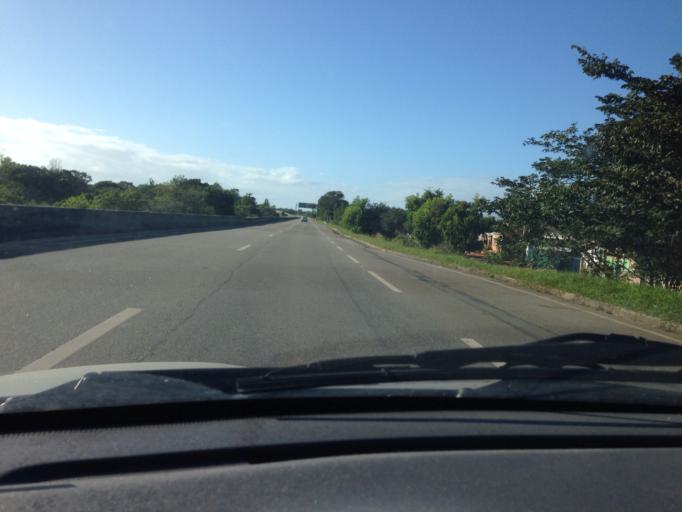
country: BR
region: Espirito Santo
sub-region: Guarapari
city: Guarapari
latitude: -20.6164
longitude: -40.4421
